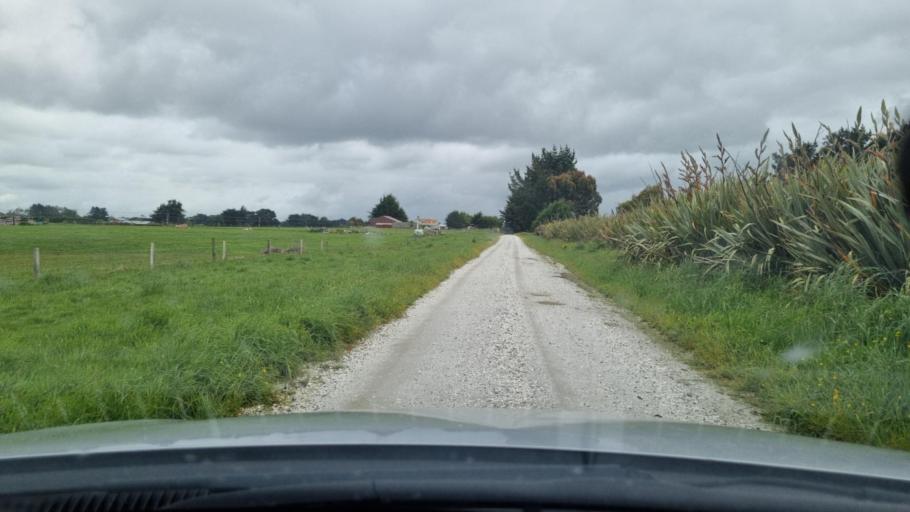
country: NZ
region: Southland
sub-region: Invercargill City
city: Invercargill
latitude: -46.4496
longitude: 168.3939
